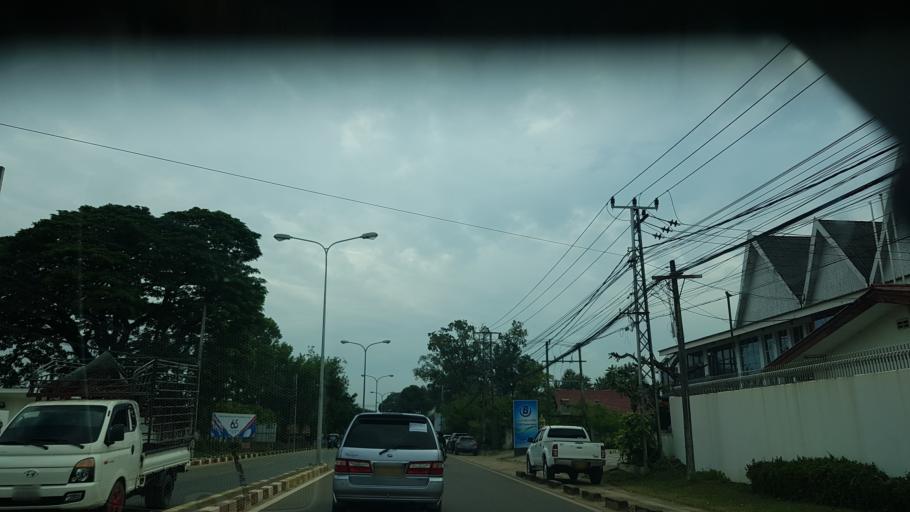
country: LA
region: Vientiane
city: Vientiane
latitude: 17.9358
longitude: 102.6173
